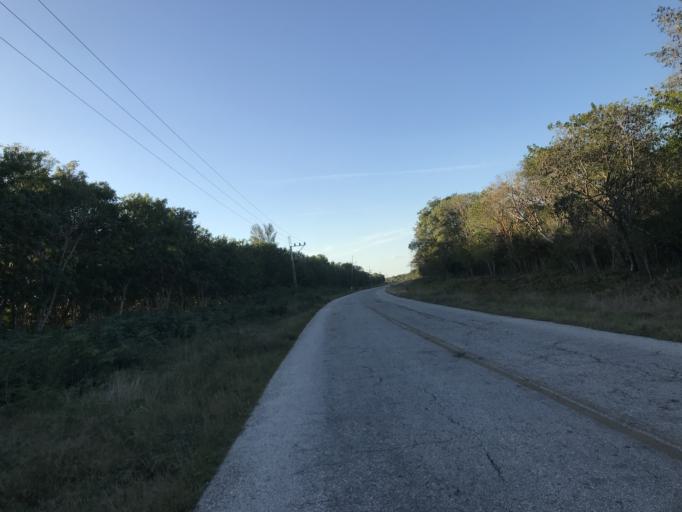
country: CU
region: Cienfuegos
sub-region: Municipio de Aguada de Pasajeros
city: Aguada de Pasajeros
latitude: 22.0698
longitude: -81.0528
